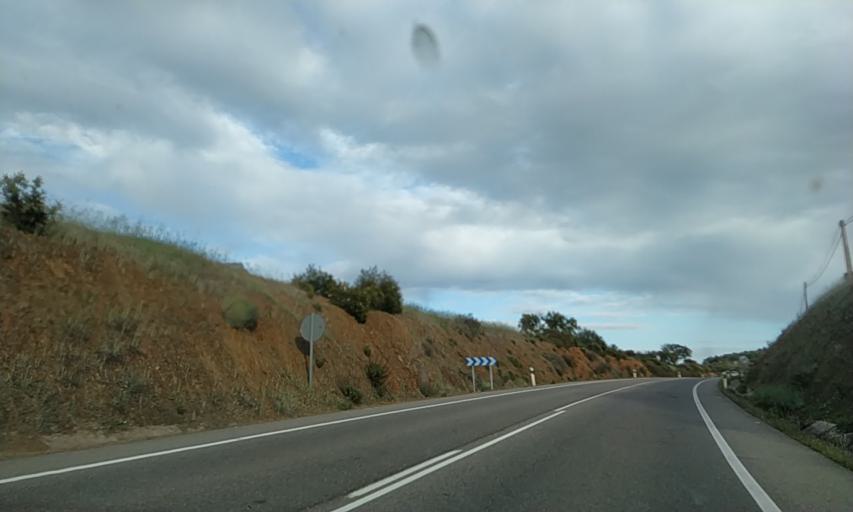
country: ES
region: Extremadura
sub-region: Provincia de Caceres
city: Canaveral
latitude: 39.8256
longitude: -6.3741
